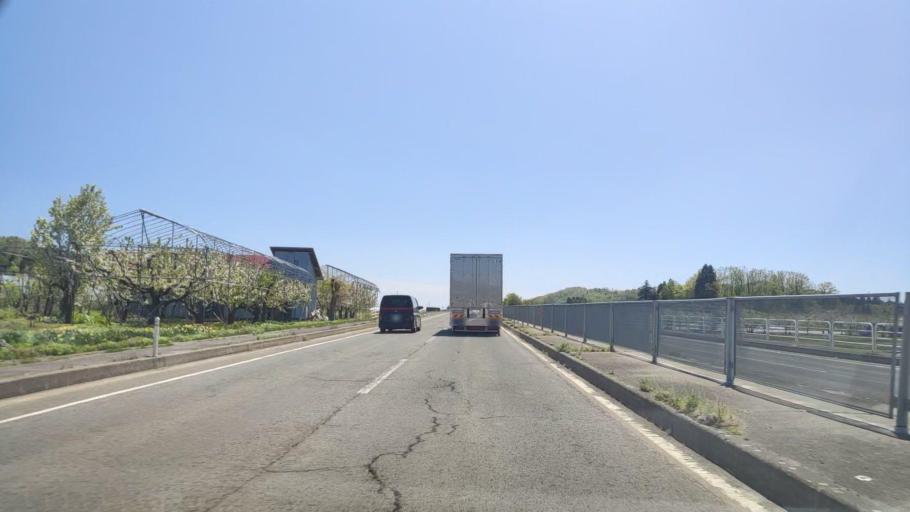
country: JP
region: Yamagata
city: Obanazawa
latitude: 38.5371
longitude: 140.3941
